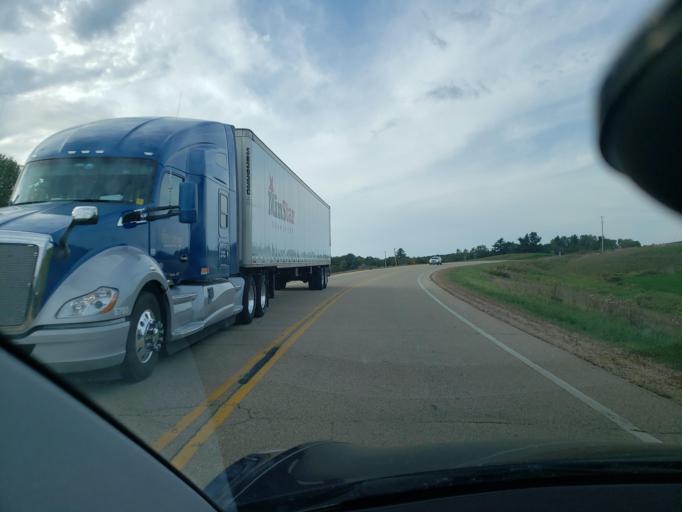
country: US
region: Wisconsin
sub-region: Waupaca County
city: Marion
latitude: 44.7396
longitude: -88.8980
